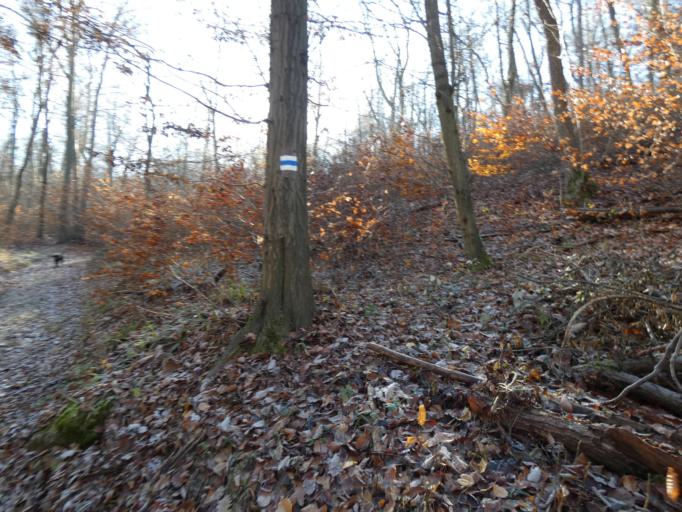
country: HU
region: Pest
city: Pilisszentivan
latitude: 47.5931
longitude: 18.8561
